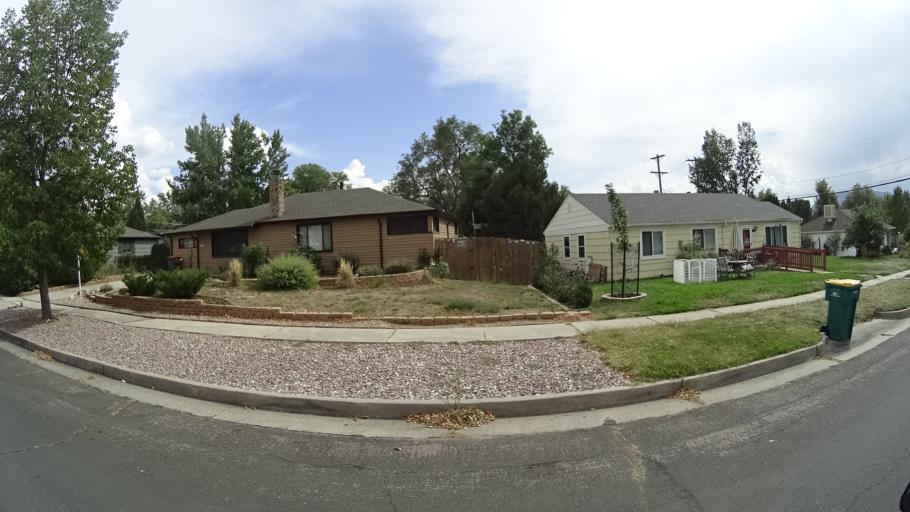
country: US
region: Colorado
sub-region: El Paso County
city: Colorado Springs
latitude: 38.8624
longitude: -104.7907
